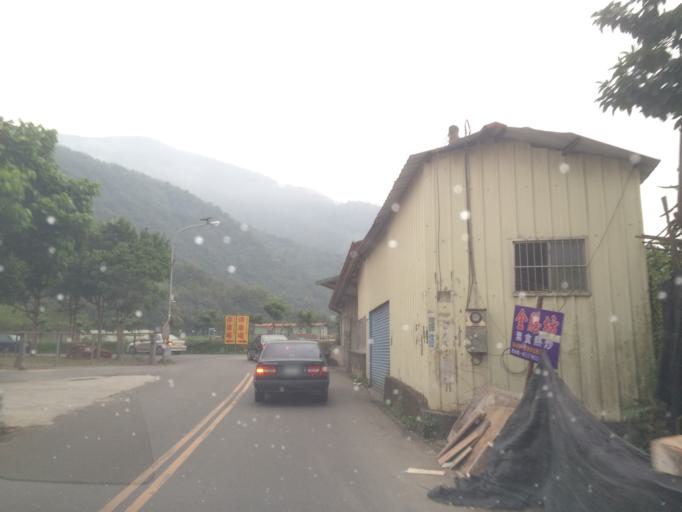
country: TW
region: Taiwan
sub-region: Nantou
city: Puli
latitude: 23.9496
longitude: 120.9859
